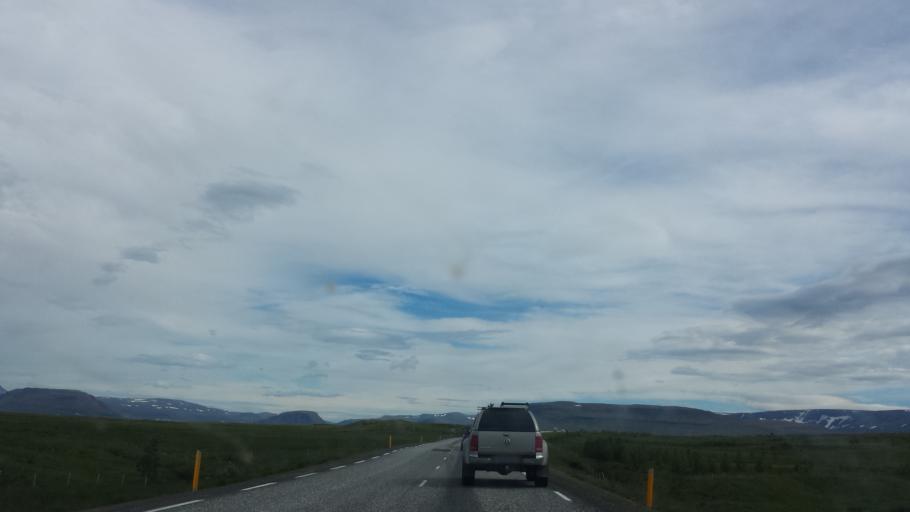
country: IS
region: West
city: Borgarnes
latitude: 64.3752
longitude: -21.8462
